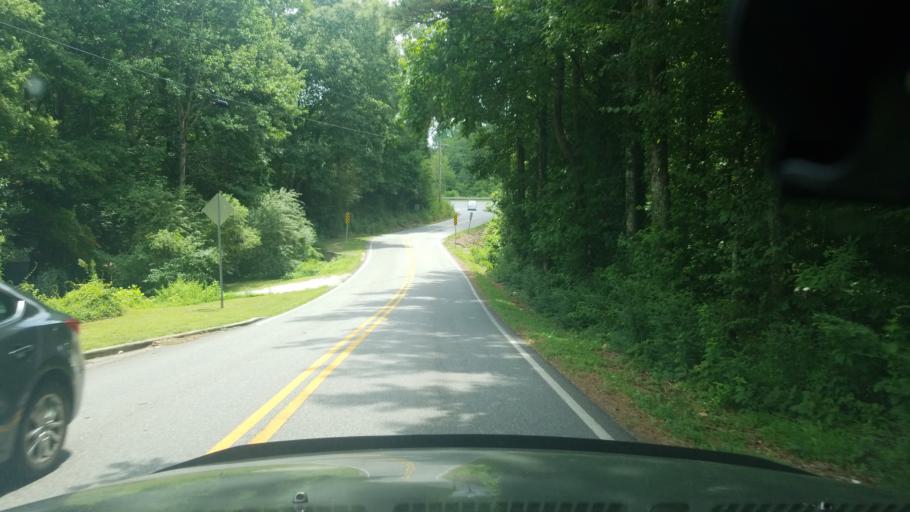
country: US
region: Georgia
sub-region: Fulton County
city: Johns Creek
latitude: 34.1040
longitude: -84.1585
